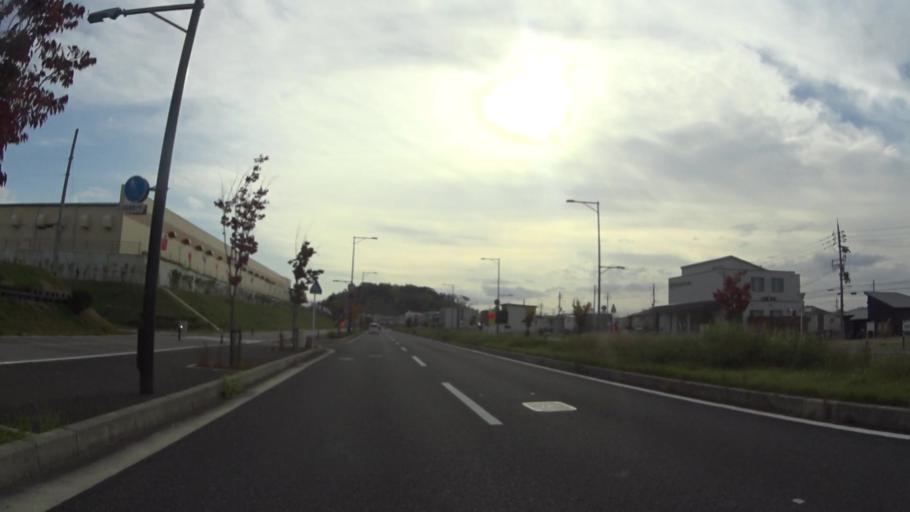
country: JP
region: Nara
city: Nara-shi
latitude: 34.7377
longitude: 135.8345
